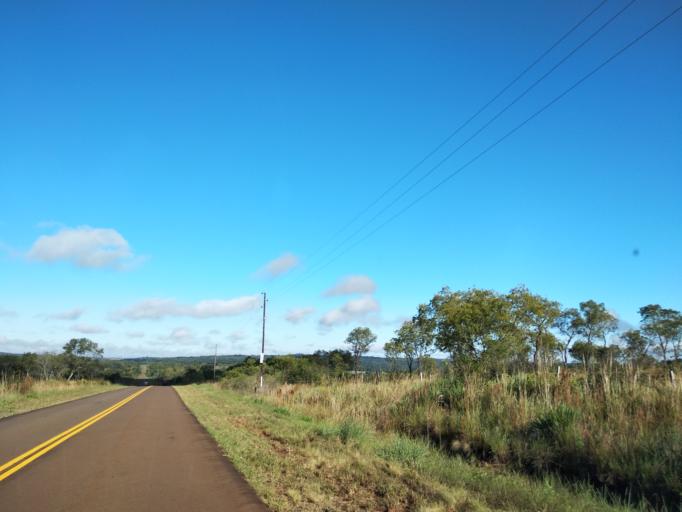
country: AR
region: Misiones
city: Santa Ana
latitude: -27.4087
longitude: -55.5535
